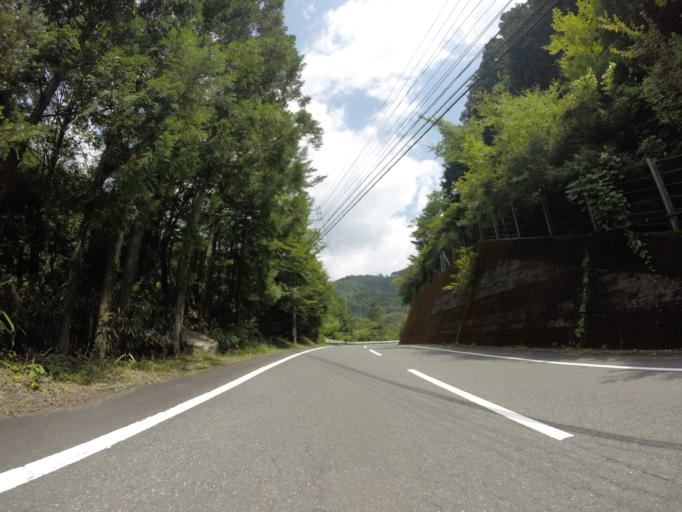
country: JP
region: Shizuoka
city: Fujinomiya
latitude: 35.2709
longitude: 138.3262
